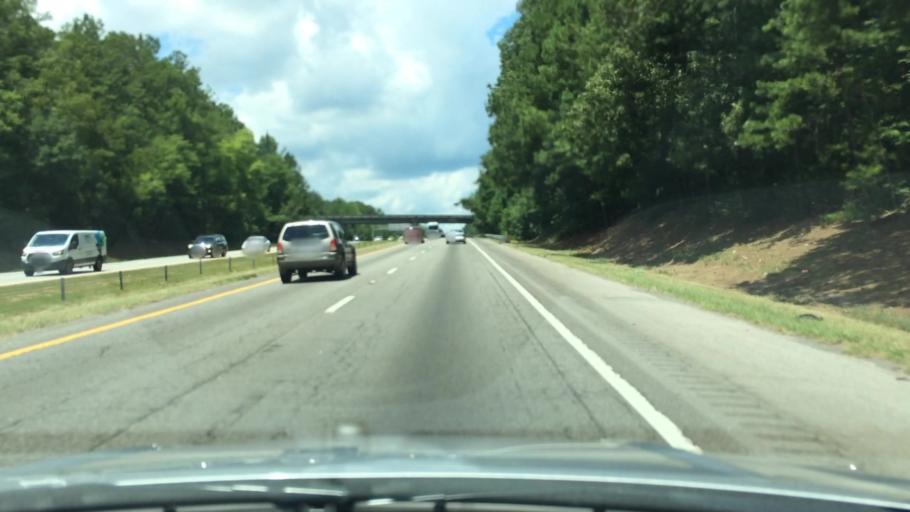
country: US
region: South Carolina
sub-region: Lexington County
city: Chapin
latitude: 34.1912
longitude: -81.3466
